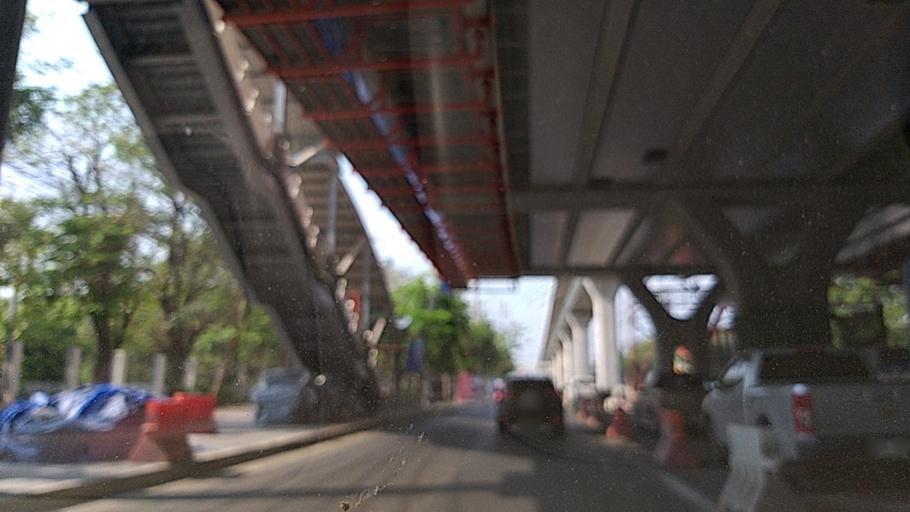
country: TH
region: Bangkok
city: Sai Mai
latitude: 13.9176
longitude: 100.6216
